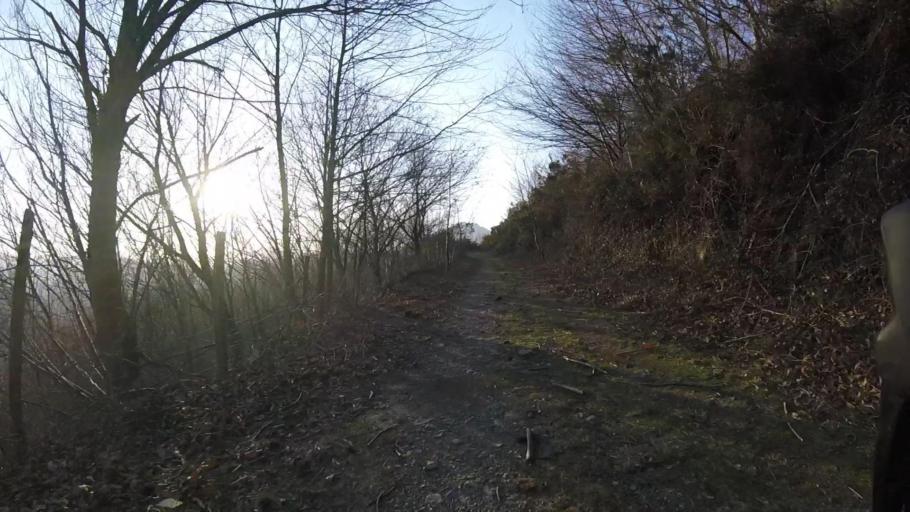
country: ES
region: Navarre
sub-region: Provincia de Navarra
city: Arano
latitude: 43.2347
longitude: -1.8650
